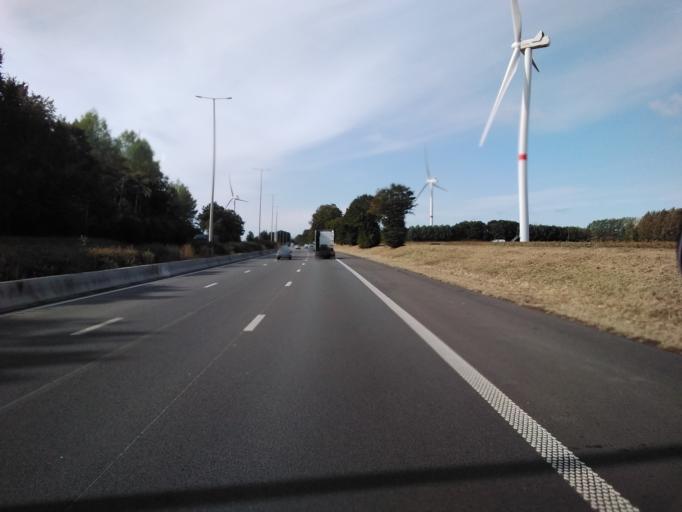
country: BE
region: Wallonia
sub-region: Province de Namur
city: Noville-les-Bois
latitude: 50.5295
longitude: 4.9349
